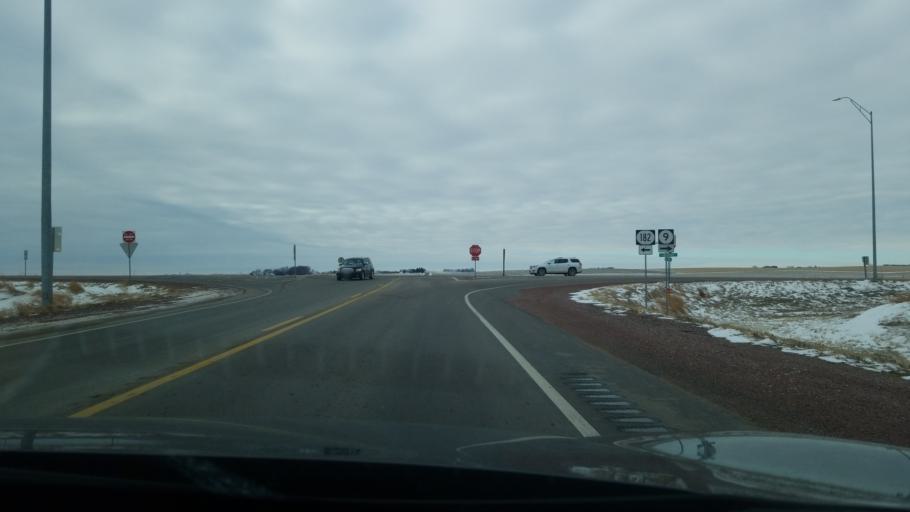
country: US
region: South Dakota
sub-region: Lincoln County
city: Canton
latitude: 43.4331
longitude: -96.4282
